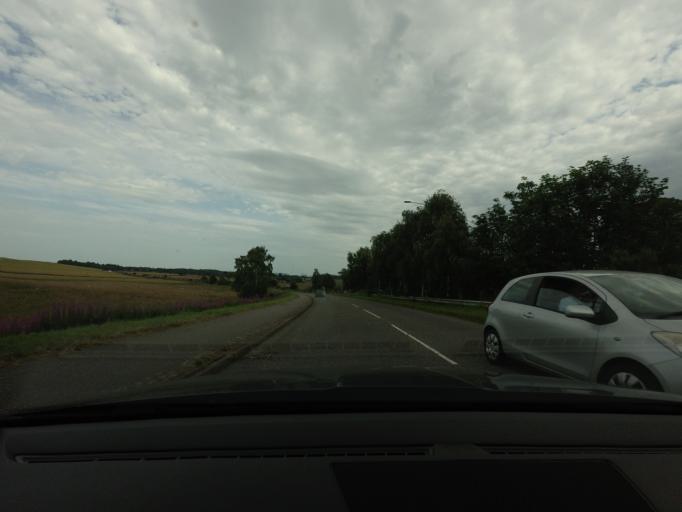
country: GB
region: Scotland
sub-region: Highland
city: Alness
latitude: 57.6836
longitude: -4.2943
